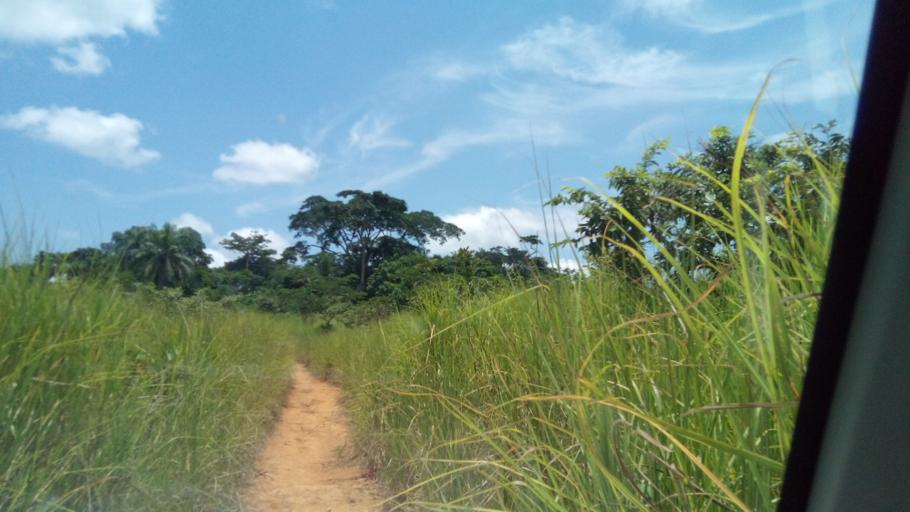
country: AO
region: Zaire
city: Mbanza Congo
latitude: -5.8055
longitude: 14.2404
